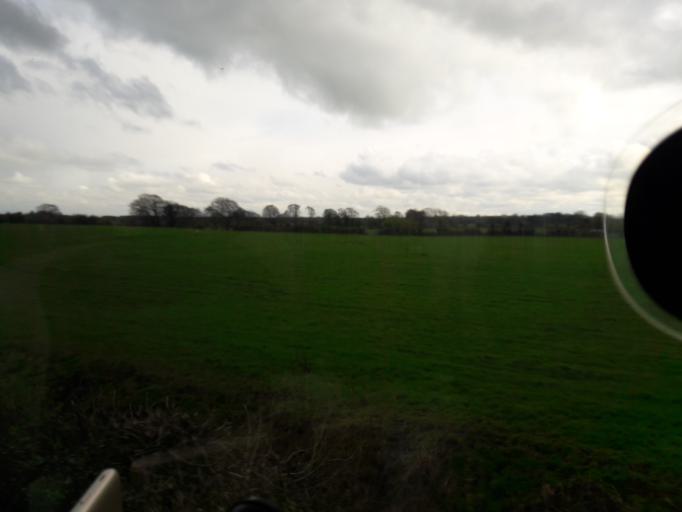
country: IE
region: Leinster
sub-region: An Iarmhi
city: Rathwire
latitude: 53.4921
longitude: -7.1480
